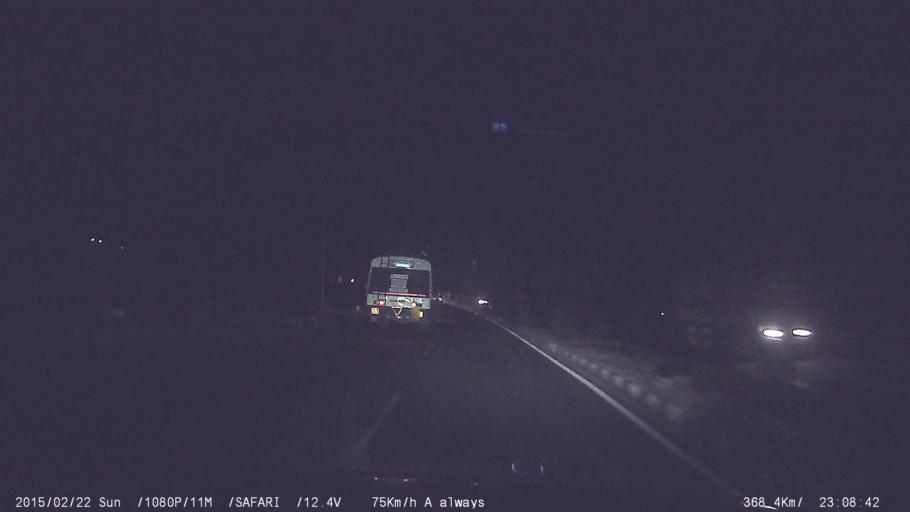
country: IN
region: Tamil Nadu
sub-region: Namakkal
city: Rasipuram
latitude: 11.4562
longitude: 78.1589
